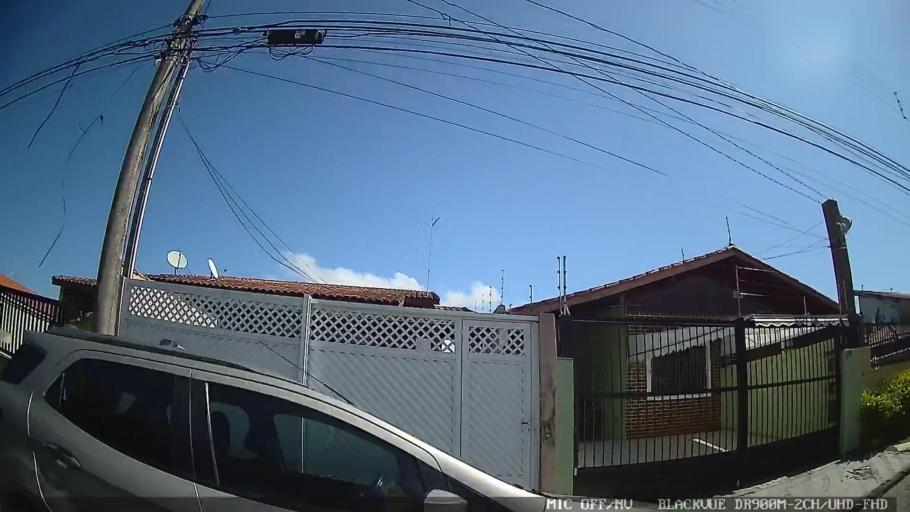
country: BR
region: Sao Paulo
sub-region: Peruibe
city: Peruibe
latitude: -24.3111
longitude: -46.9969
